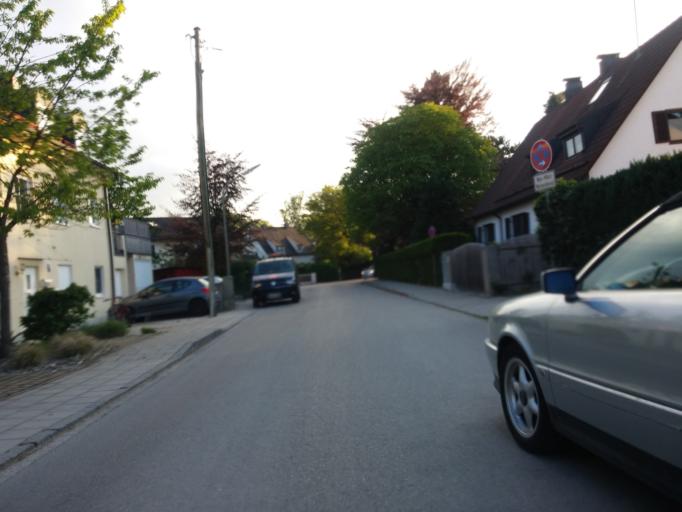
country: DE
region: Bavaria
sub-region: Upper Bavaria
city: Vaterstetten
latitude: 48.1026
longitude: 11.7774
